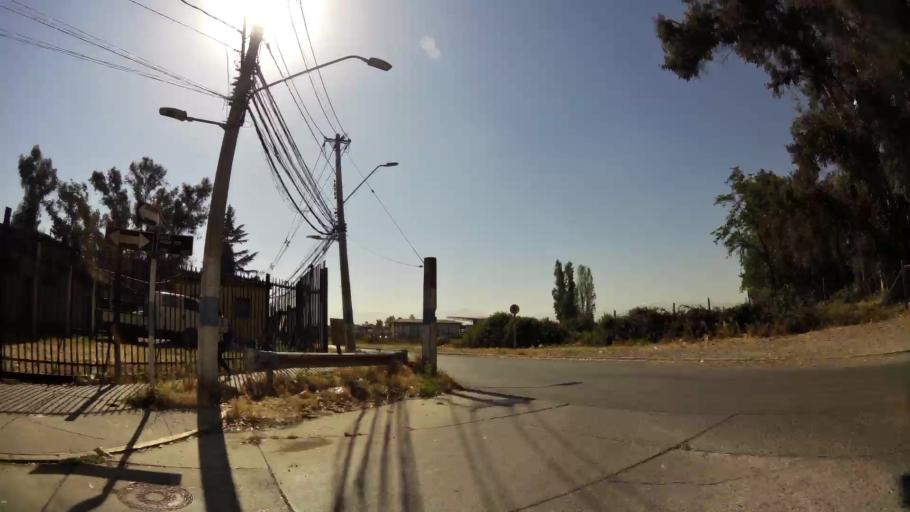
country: CL
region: Santiago Metropolitan
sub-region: Provincia de Maipo
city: San Bernardo
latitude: -33.5668
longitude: -70.7049
